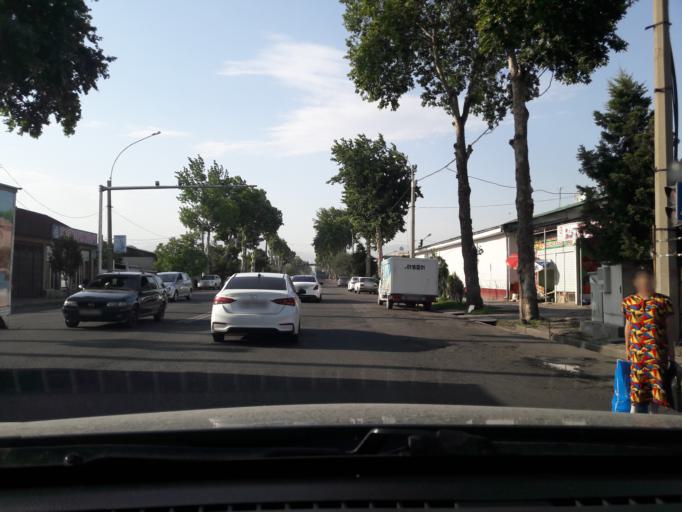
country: TJ
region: Dushanbe
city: Dushanbe
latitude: 38.5463
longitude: 68.7718
